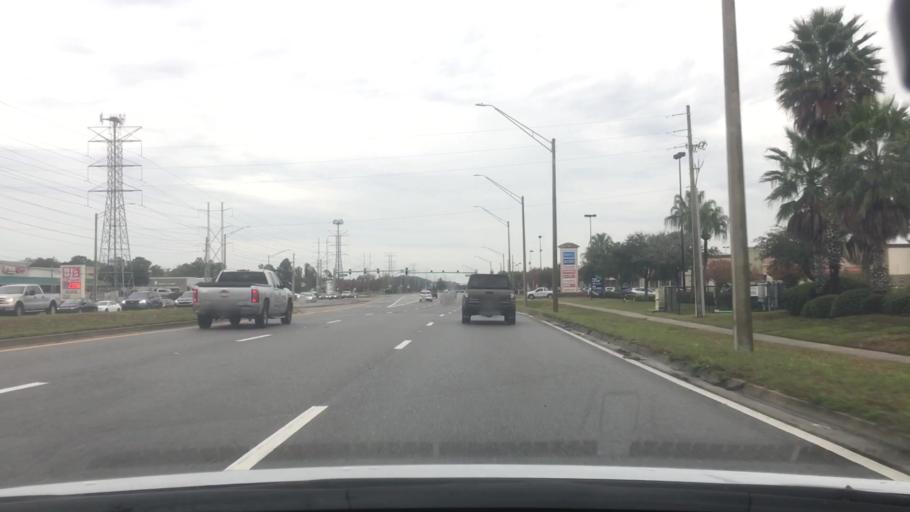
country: US
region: Florida
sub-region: Duval County
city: Atlantic Beach
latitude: 30.3190
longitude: -81.4896
